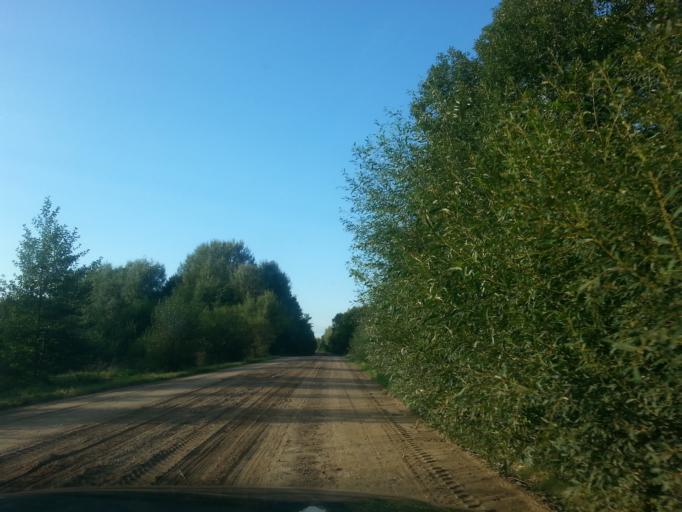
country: BY
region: Minsk
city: Narach
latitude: 55.0227
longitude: 26.6534
